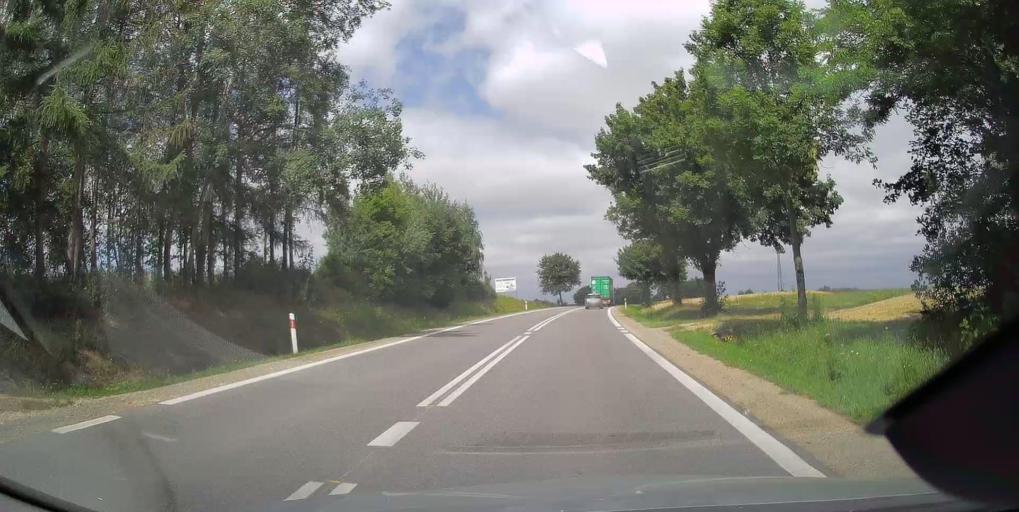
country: PL
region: Swietokrzyskie
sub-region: Powiat sandomierski
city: Klimontow
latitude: 50.6362
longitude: 21.4673
